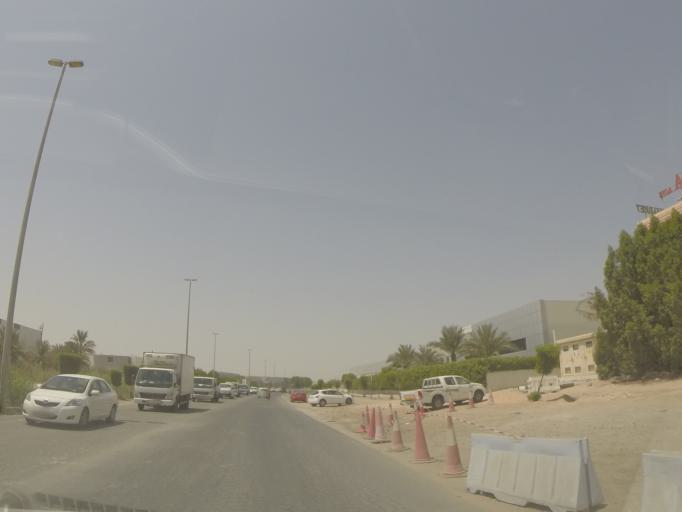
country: AE
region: Dubai
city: Dubai
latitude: 24.9847
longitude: 55.1959
